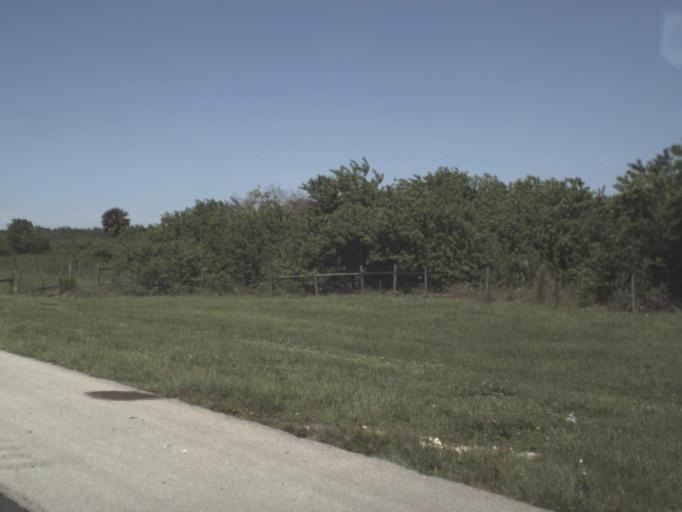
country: US
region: Florida
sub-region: Lee County
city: Bonita Springs
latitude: 26.3605
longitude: -81.7611
